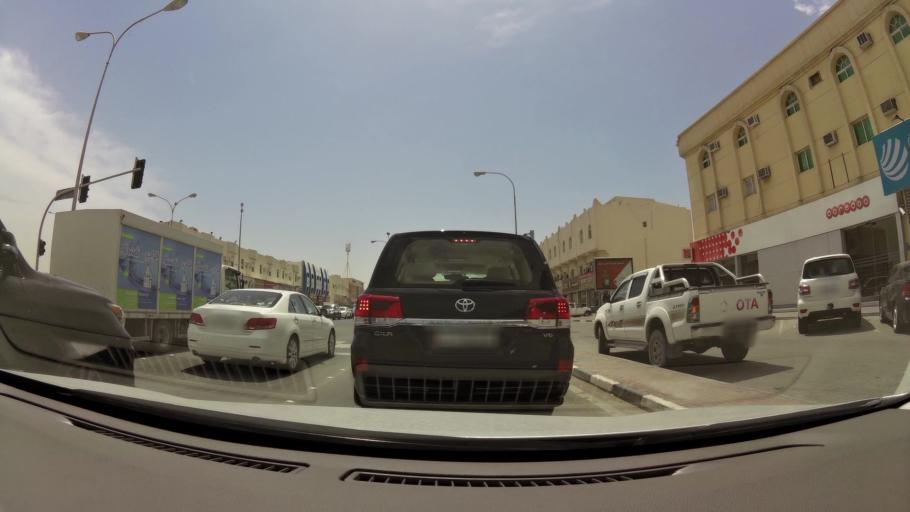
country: QA
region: Baladiyat ar Rayyan
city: Ar Rayyan
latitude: 25.2946
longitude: 51.4203
